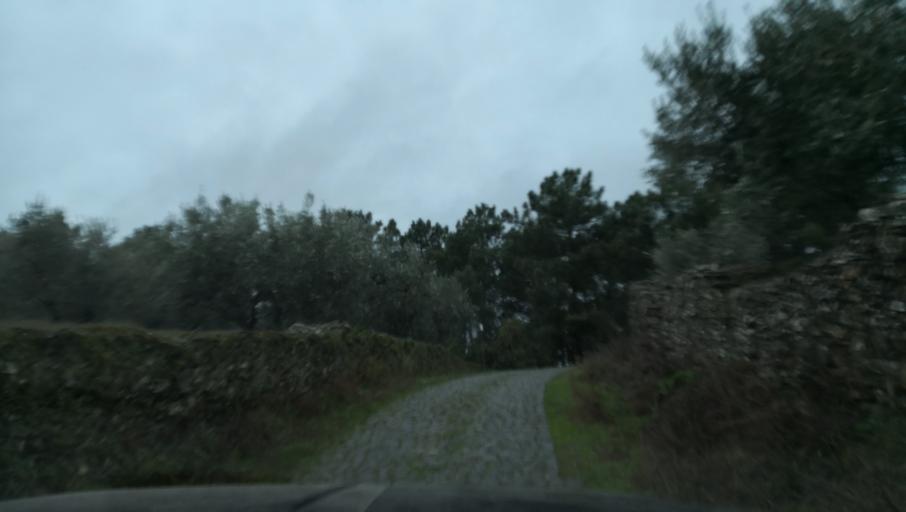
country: PT
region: Vila Real
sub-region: Vila Real
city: Vila Real
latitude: 41.2513
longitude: -7.7383
